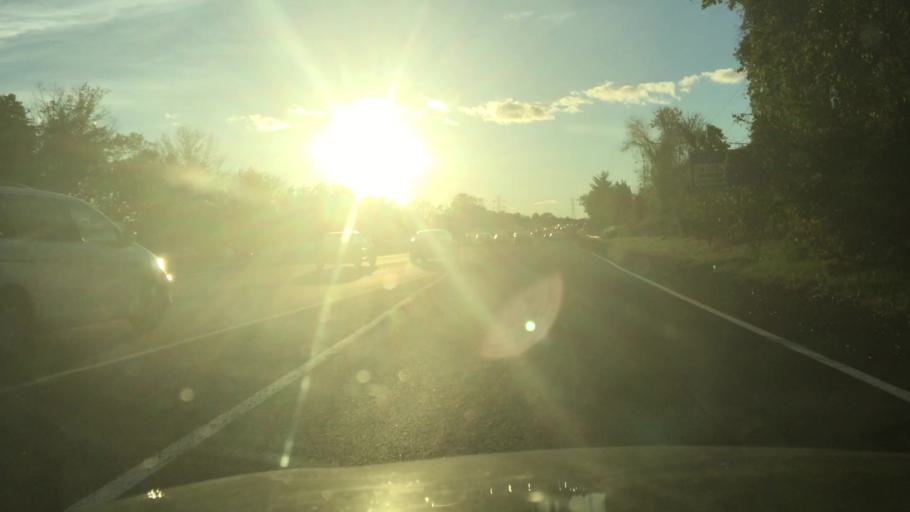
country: US
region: New Jersey
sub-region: Mercer County
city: Lawrenceville
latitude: 40.2861
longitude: -74.7163
